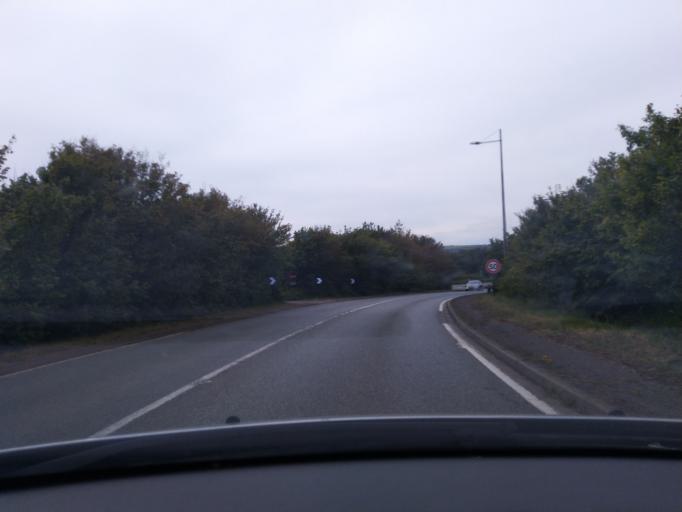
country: FR
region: Nord-Pas-de-Calais
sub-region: Departement du Pas-de-Calais
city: Marquise
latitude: 50.8277
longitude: 1.6937
